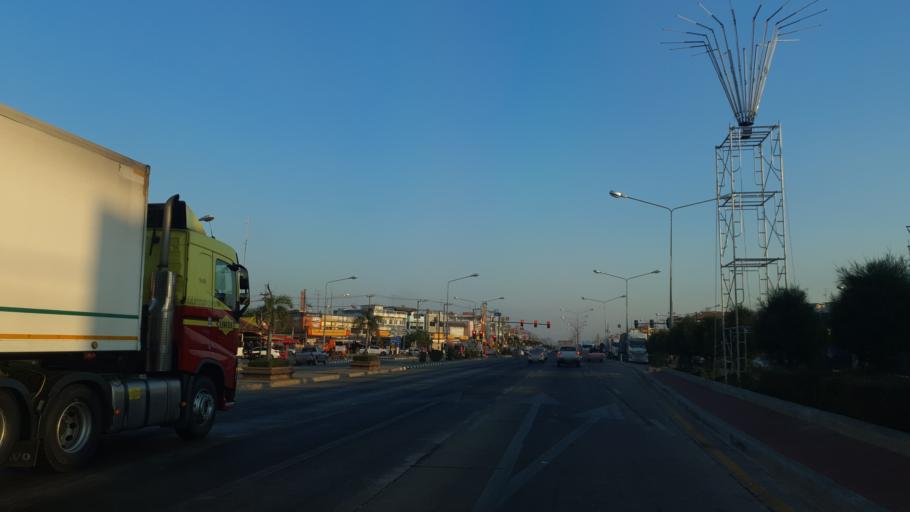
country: TH
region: Kamphaeng Phet
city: Khanu Woralaksaburi
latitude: 16.0002
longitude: 99.8042
